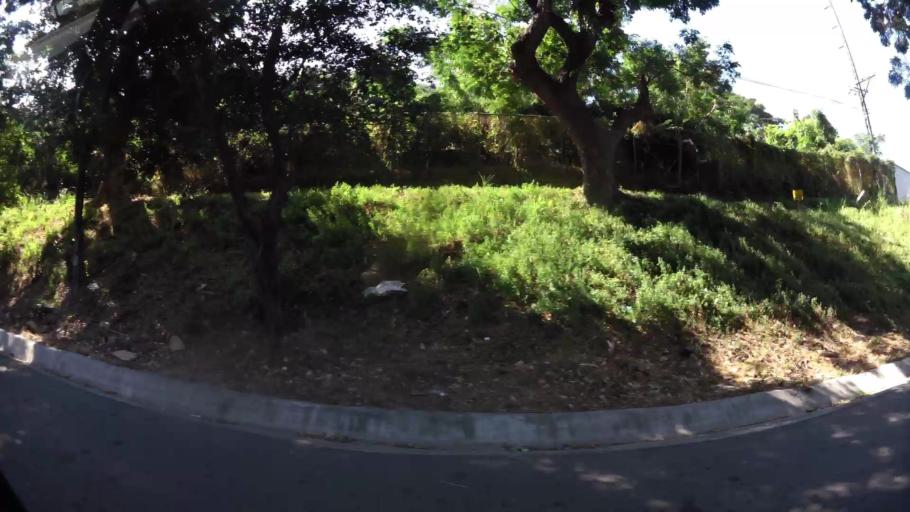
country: EC
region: Guayas
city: Santa Lucia
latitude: -2.1865
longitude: -79.9625
